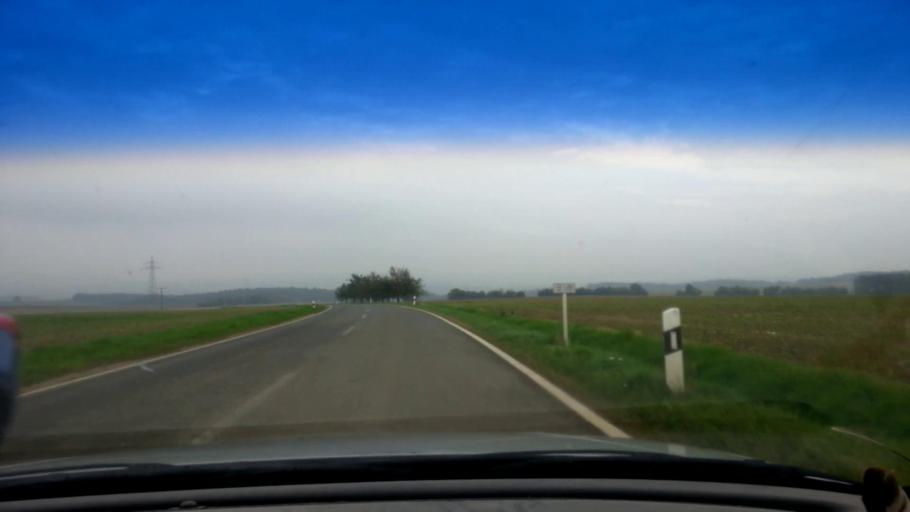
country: DE
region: Bavaria
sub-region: Upper Franconia
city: Ebensfeld
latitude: 50.0669
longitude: 10.9091
